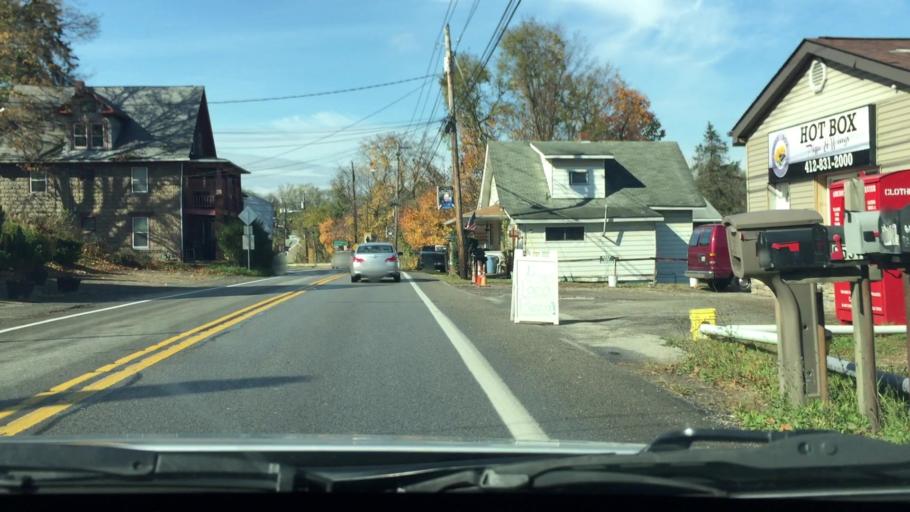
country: US
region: Pennsylvania
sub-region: Allegheny County
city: South Park Township
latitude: 40.2869
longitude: -80.0238
